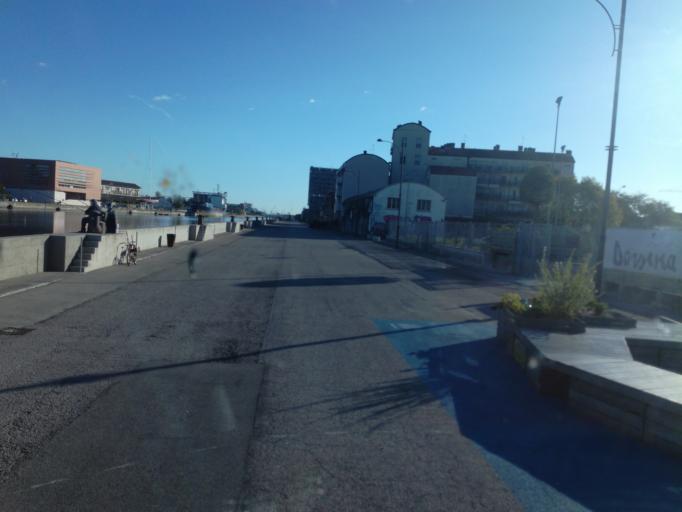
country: IT
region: Emilia-Romagna
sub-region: Provincia di Ravenna
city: Ravenna
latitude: 44.4204
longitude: 12.2108
